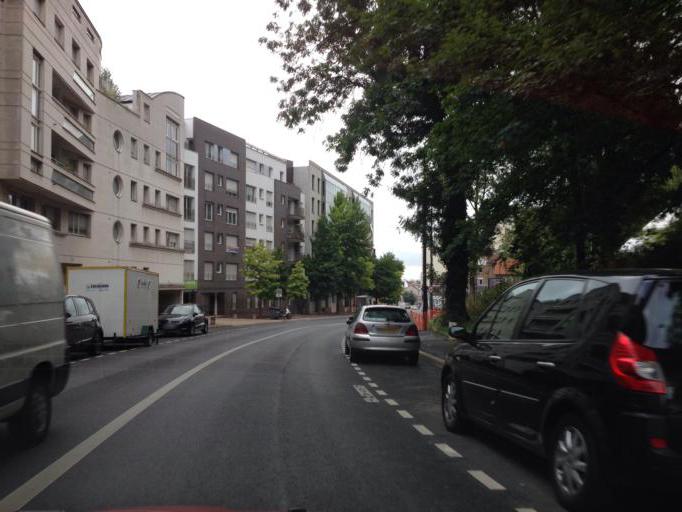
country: FR
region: Ile-de-France
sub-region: Departement des Hauts-de-Seine
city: Boulogne-Billancourt
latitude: 48.8186
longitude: 2.2578
